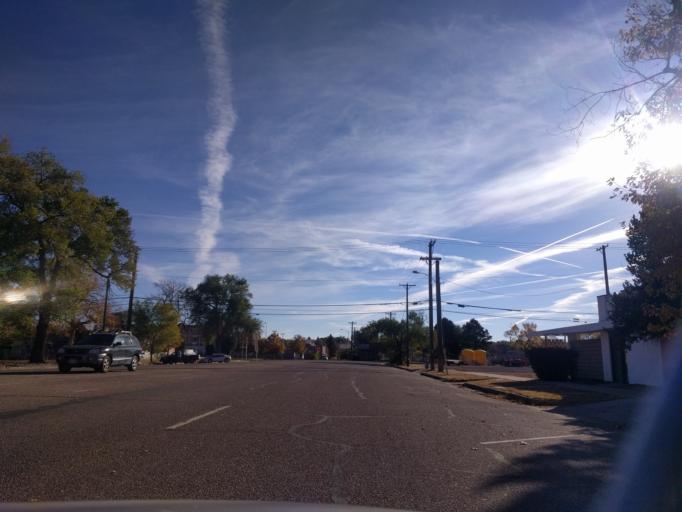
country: US
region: Colorado
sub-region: El Paso County
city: Colorado Springs
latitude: 38.8295
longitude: -104.8200
